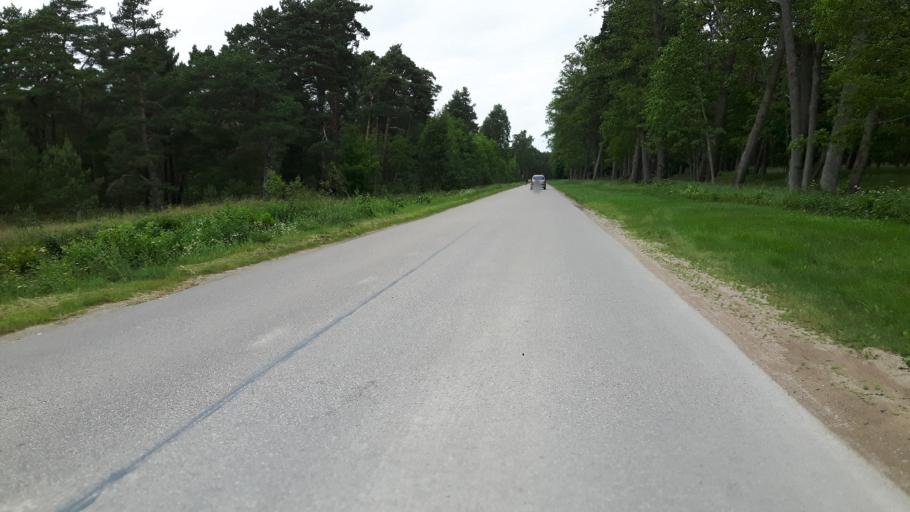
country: LV
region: Liepaja
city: Vec-Liepaja
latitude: 56.5637
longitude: 21.0147
